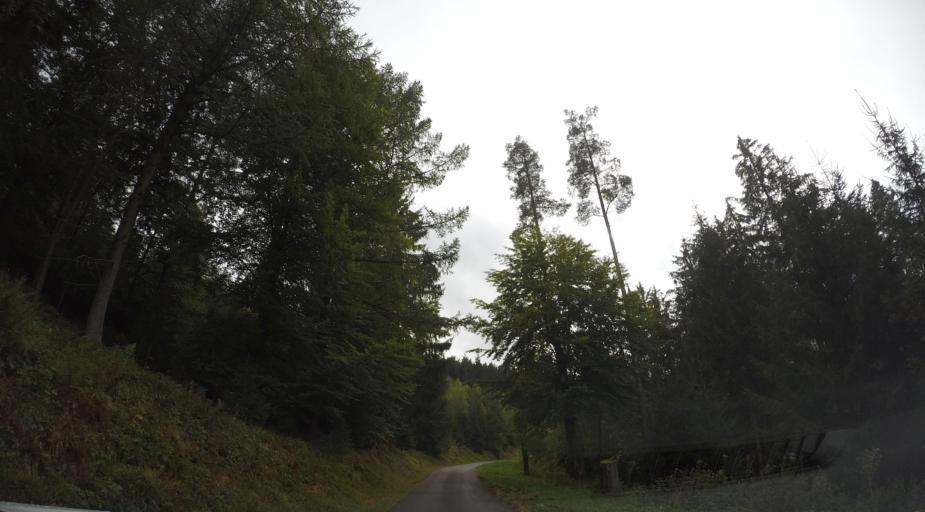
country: DE
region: Baden-Wuerttemberg
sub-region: Karlsruhe Region
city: Baiersbronn
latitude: 48.4909
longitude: 8.3121
